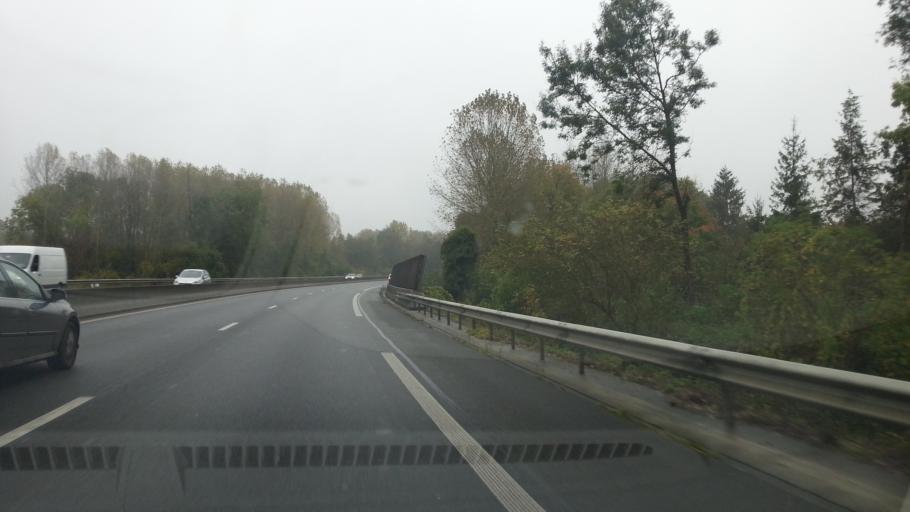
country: FR
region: Picardie
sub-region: Departement de l'Oise
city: Cauffry
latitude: 49.3081
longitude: 2.4527
